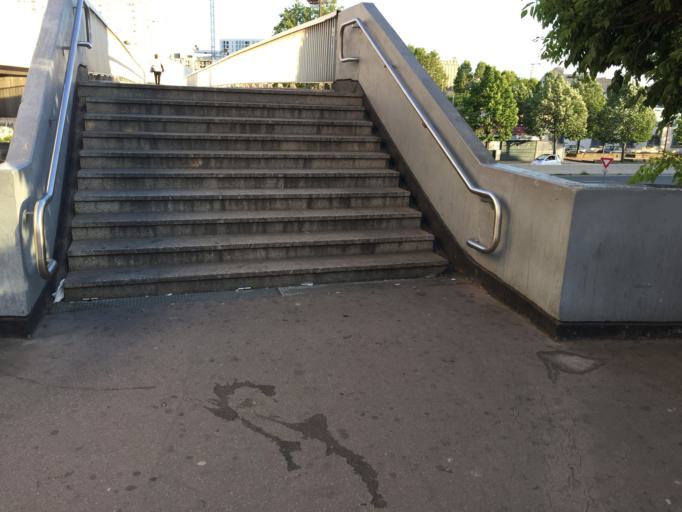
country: FR
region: Provence-Alpes-Cote d'Azur
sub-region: Departement des Bouches-du-Rhone
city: Marseille 03
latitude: 43.3204
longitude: 5.3713
